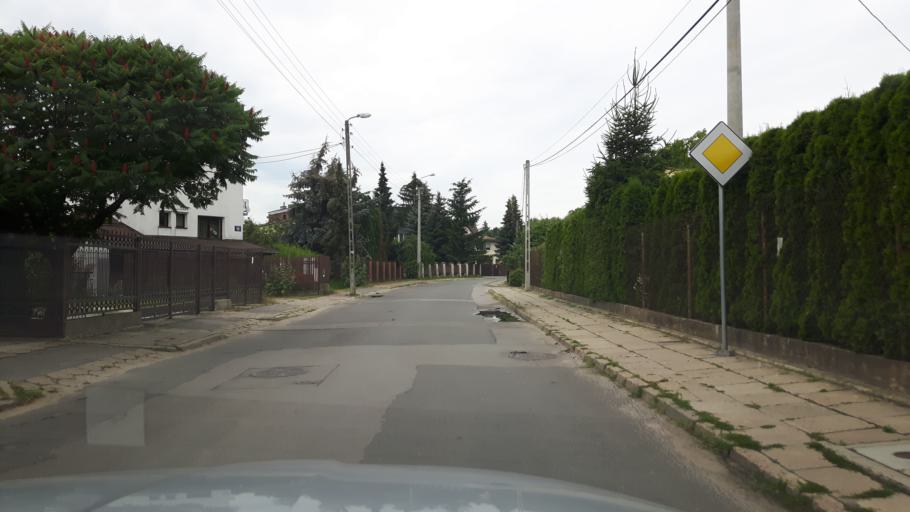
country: PL
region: Masovian Voivodeship
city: Zielonka
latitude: 52.3125
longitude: 21.1620
